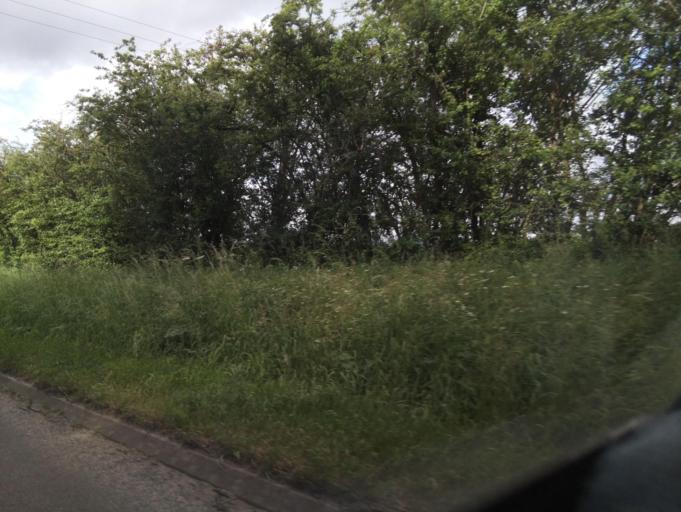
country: GB
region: England
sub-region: Dudley
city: Kingswinford
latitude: 52.4446
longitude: -2.2114
